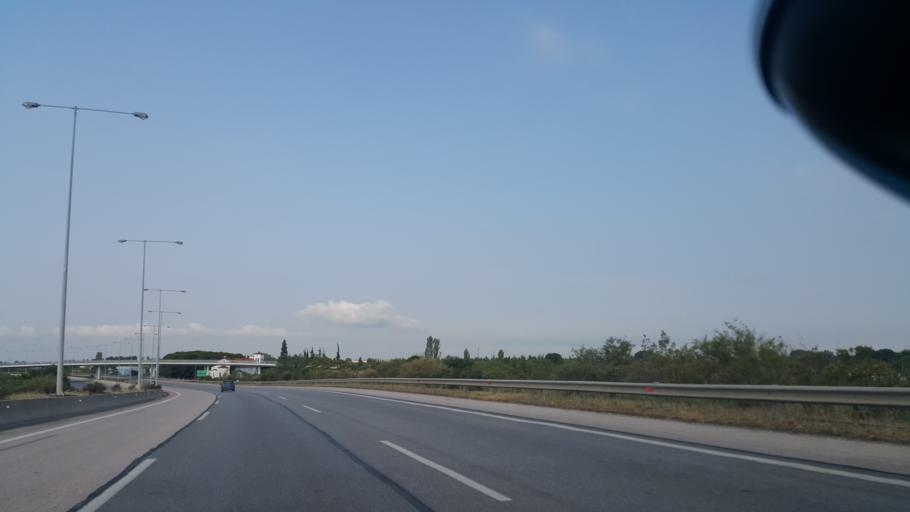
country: GR
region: Central Macedonia
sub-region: Nomos Thessalonikis
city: Nea Magnisia
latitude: 40.6909
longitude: 22.8387
